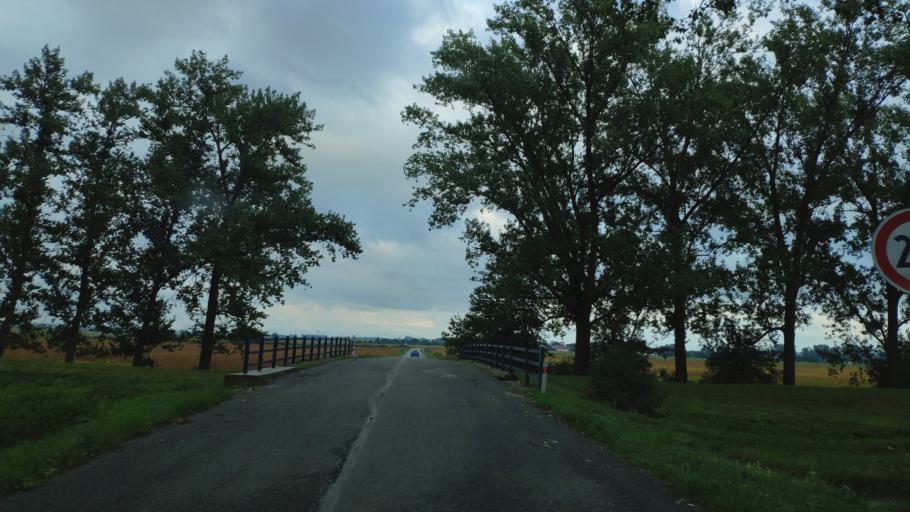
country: SK
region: Kosicky
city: Moldava nad Bodvou
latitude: 48.5821
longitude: 20.9352
